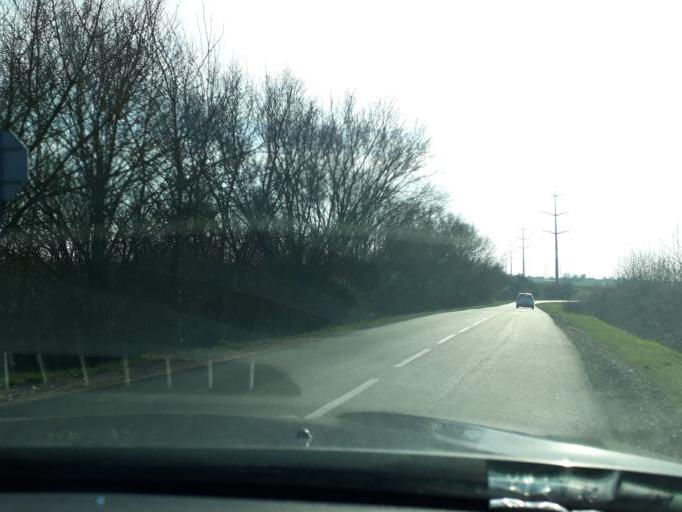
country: FR
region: Centre
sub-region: Departement du Loiret
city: Meung-sur-Loire
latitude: 47.8476
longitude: 1.6823
